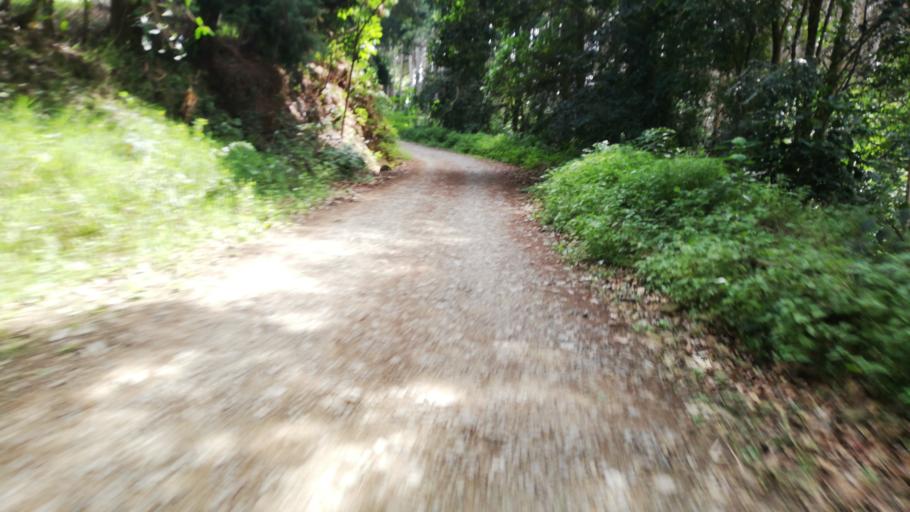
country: CO
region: Valle del Cauca
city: Yumbo
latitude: 3.6339
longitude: -76.5464
